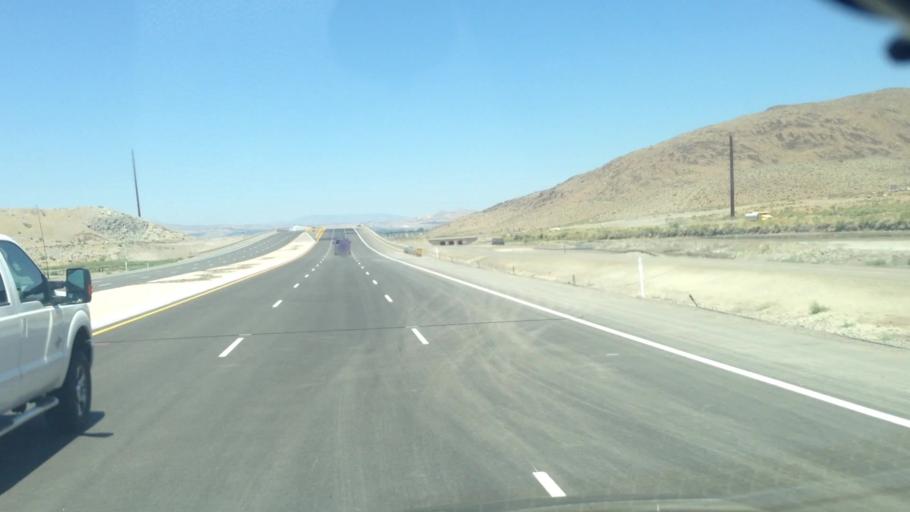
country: US
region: Nevada
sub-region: Washoe County
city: Sparks
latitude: 39.4629
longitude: -119.7269
